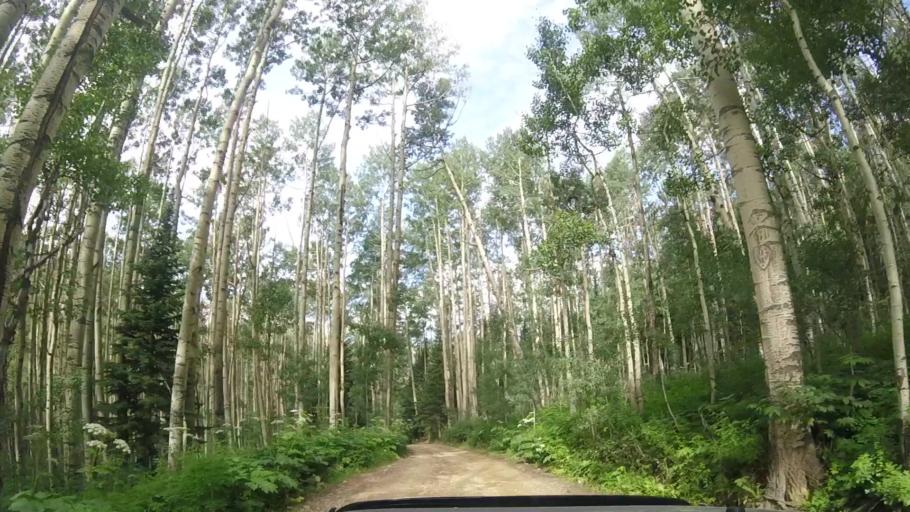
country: US
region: Colorado
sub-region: San Miguel County
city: Telluride
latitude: 37.8590
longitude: -107.8076
